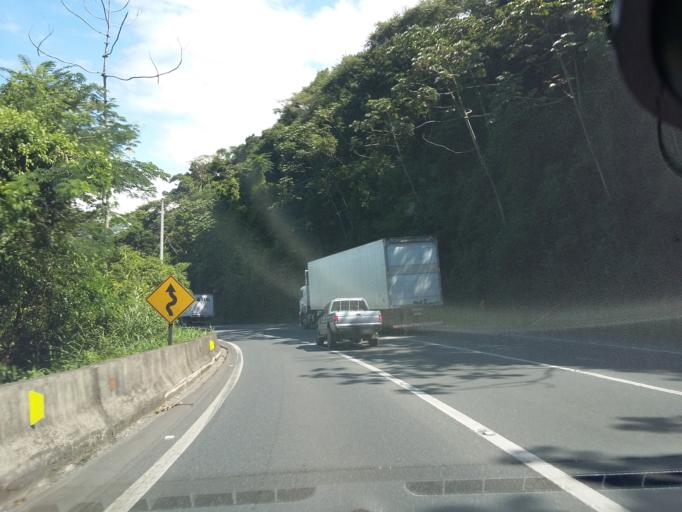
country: BR
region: Santa Catarina
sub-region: Itapema
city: Itapema
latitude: -27.0452
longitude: -48.5995
